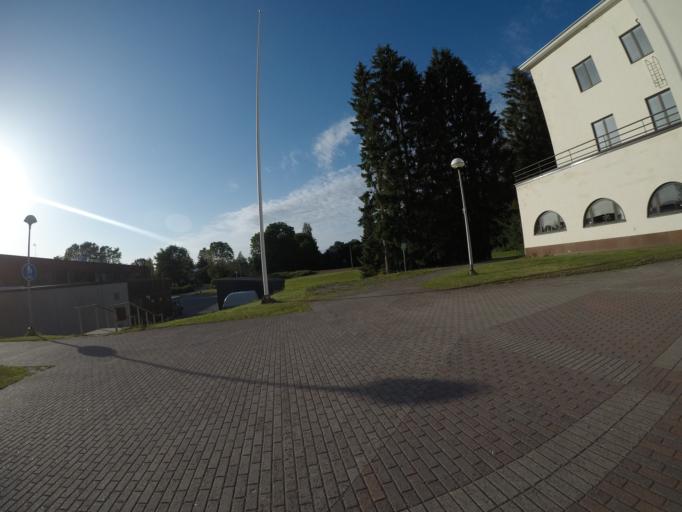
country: FI
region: Haeme
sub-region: Haemeenlinna
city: Haemeenlinna
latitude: 60.9865
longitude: 24.4439
